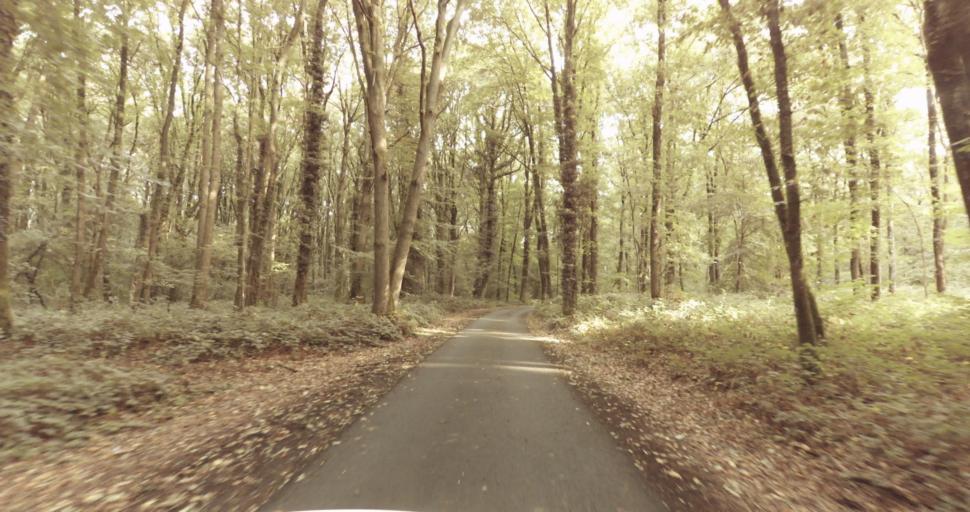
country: FR
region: Lower Normandy
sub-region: Departement de l'Orne
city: Vimoutiers
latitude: 48.9227
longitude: 0.1482
